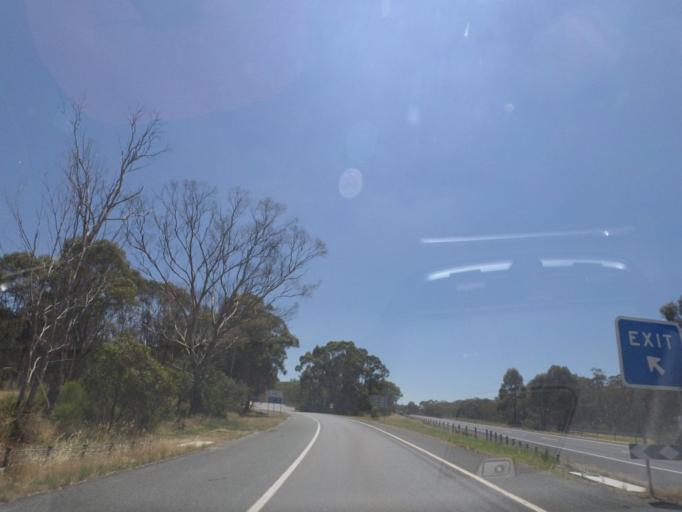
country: AU
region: Victoria
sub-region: Murrindindi
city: Kinglake West
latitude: -36.9649
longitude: 145.1806
